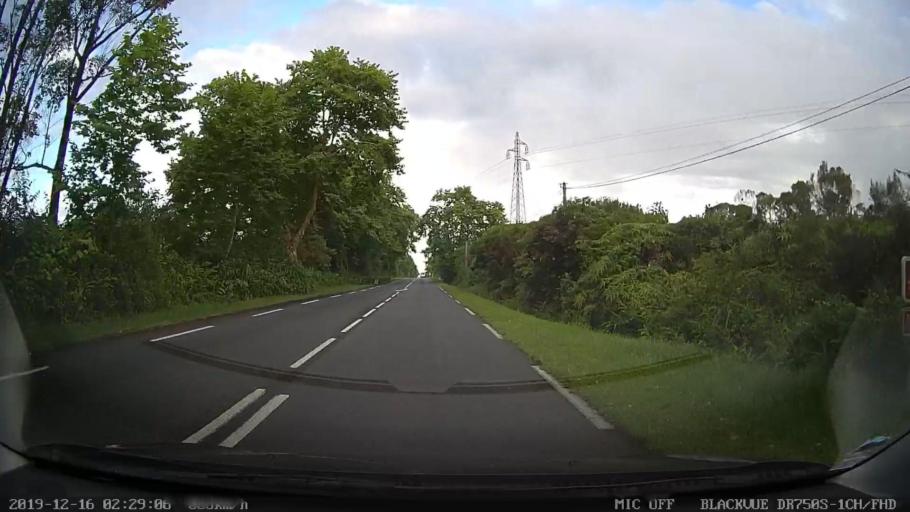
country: RE
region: Reunion
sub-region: Reunion
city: Saint-Benoit
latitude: -21.1158
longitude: 55.6489
